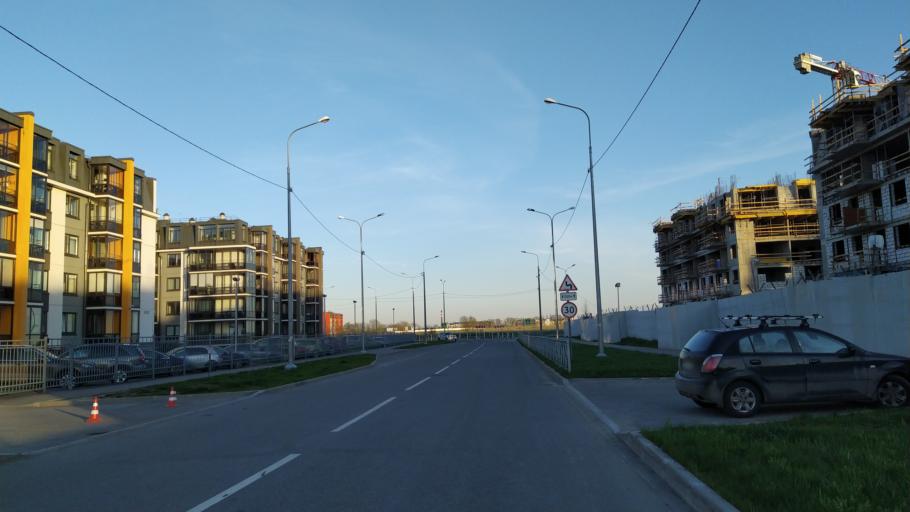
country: RU
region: St.-Petersburg
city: Pushkin
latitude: 59.7002
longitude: 30.4013
